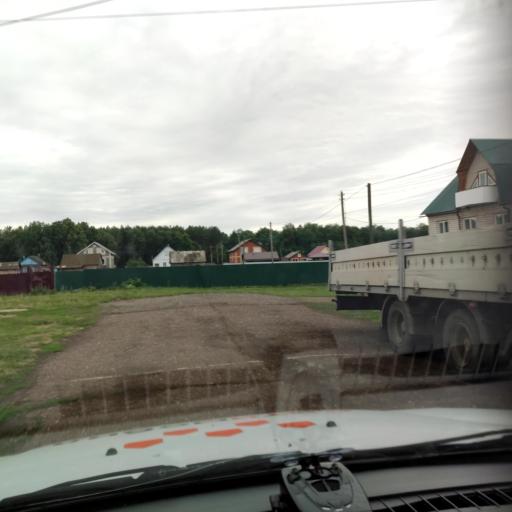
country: RU
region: Bashkortostan
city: Kabakovo
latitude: 54.4552
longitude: 55.9534
